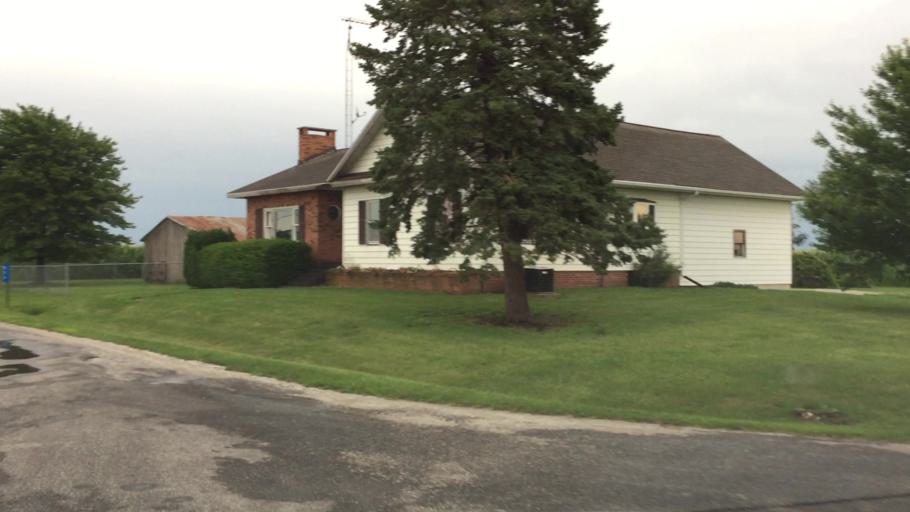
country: US
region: Illinois
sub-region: Hancock County
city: Hamilton
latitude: 40.3633
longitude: -91.3421
